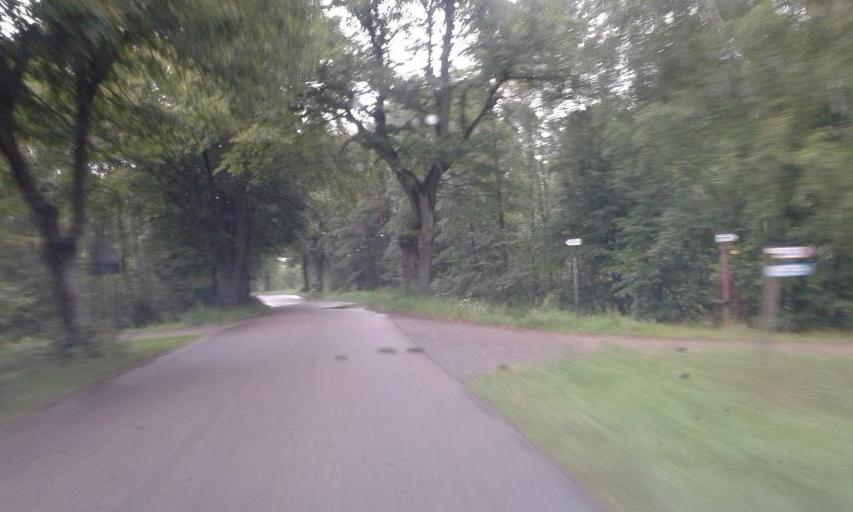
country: PL
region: West Pomeranian Voivodeship
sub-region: Powiat szczecinecki
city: Borne Sulinowo
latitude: 53.5002
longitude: 16.5004
